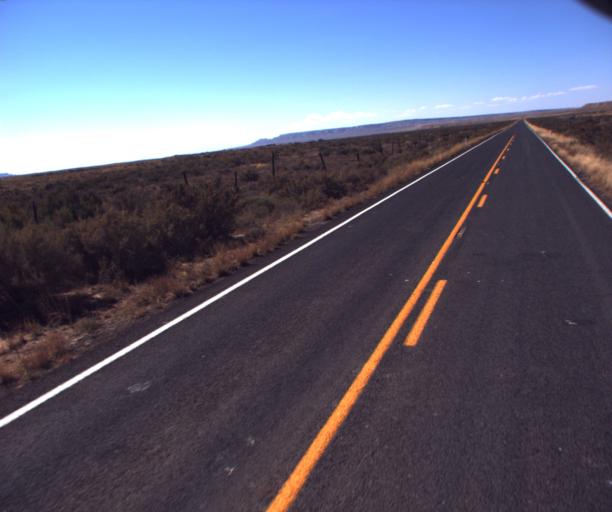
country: US
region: Arizona
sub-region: Navajo County
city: First Mesa
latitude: 35.9838
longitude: -110.7122
